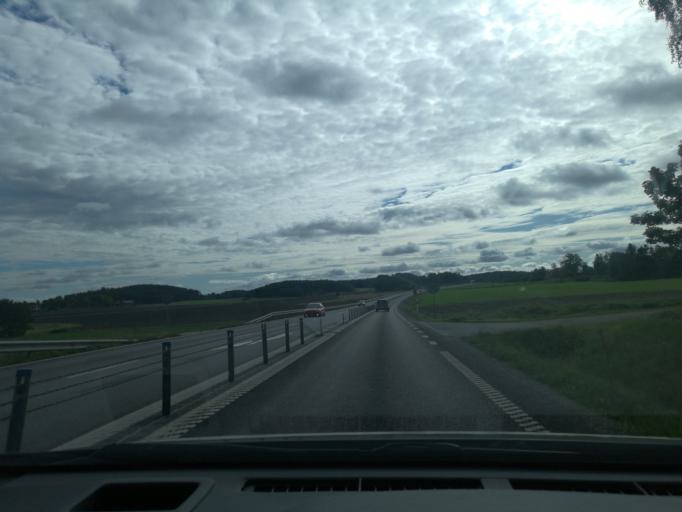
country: SE
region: OEstergoetland
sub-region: Soderkopings Kommun
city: Soederkoeping
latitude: 58.5393
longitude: 16.2769
